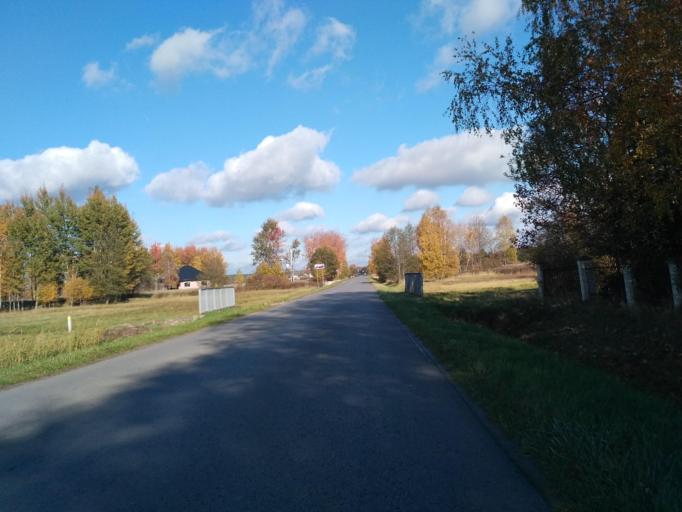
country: PL
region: Subcarpathian Voivodeship
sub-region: Powiat rzeszowski
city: Swilcza
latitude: 50.1214
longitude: 21.9005
